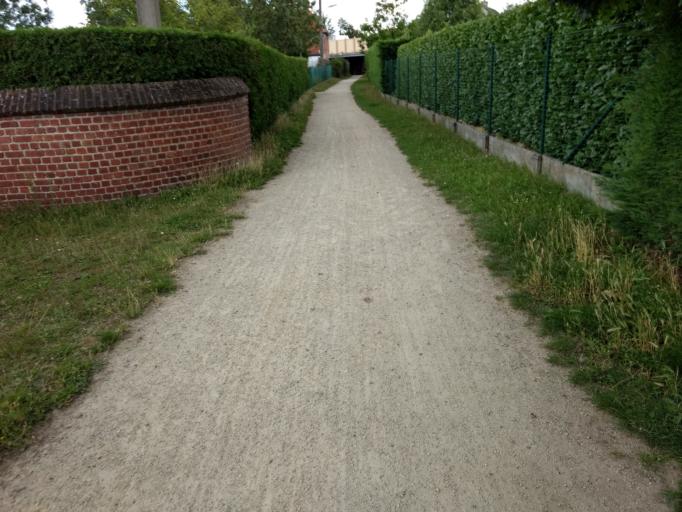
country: BE
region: Flanders
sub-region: Provincie Oost-Vlaanderen
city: Sint-Martens-Latem
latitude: 51.0237
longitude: 3.6710
